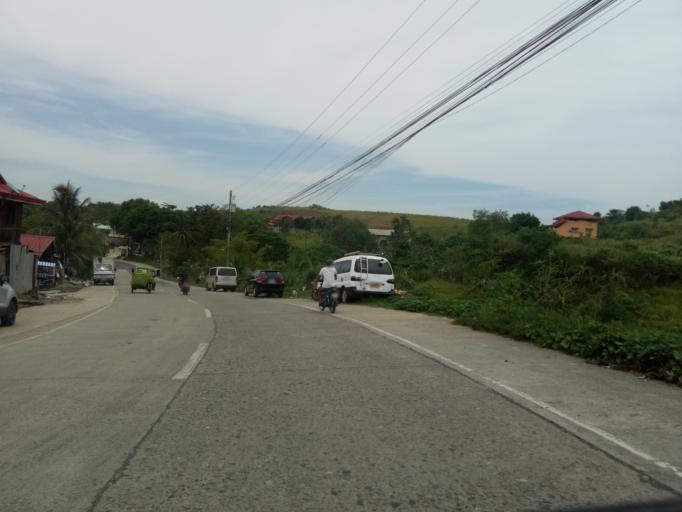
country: PH
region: Caraga
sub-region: Province of Surigao del Norte
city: Surigao
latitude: 9.7726
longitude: 125.4913
